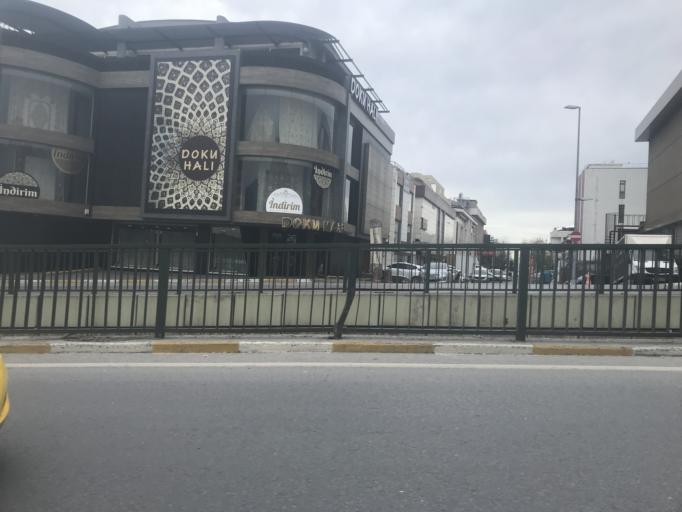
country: TR
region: Istanbul
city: Umraniye
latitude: 40.9981
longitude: 29.1550
